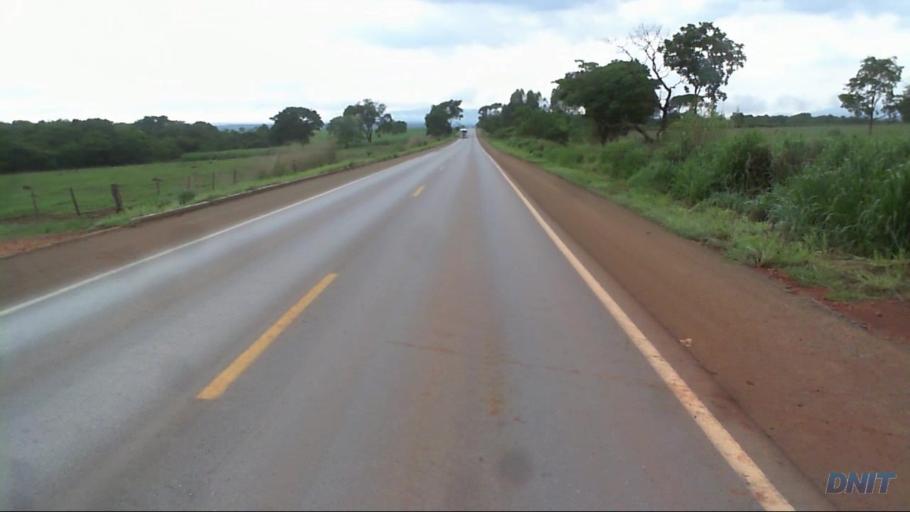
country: BR
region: Goias
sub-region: Uruacu
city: Uruacu
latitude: -14.7087
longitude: -49.1111
